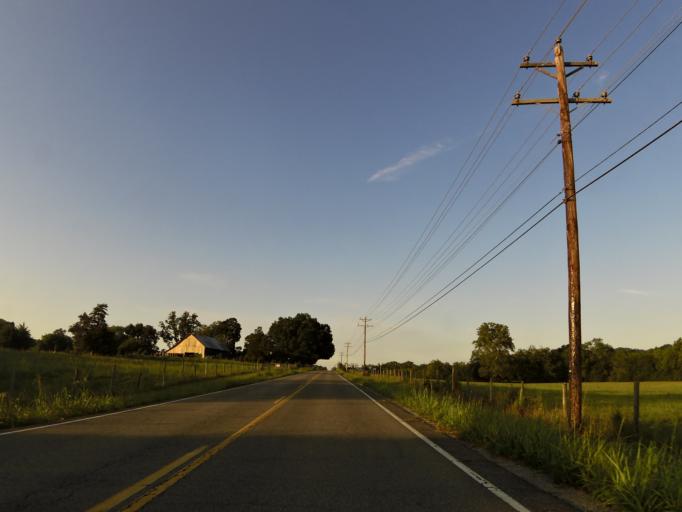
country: US
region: Tennessee
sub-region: Roane County
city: Rockwood
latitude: 35.6973
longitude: -84.6556
